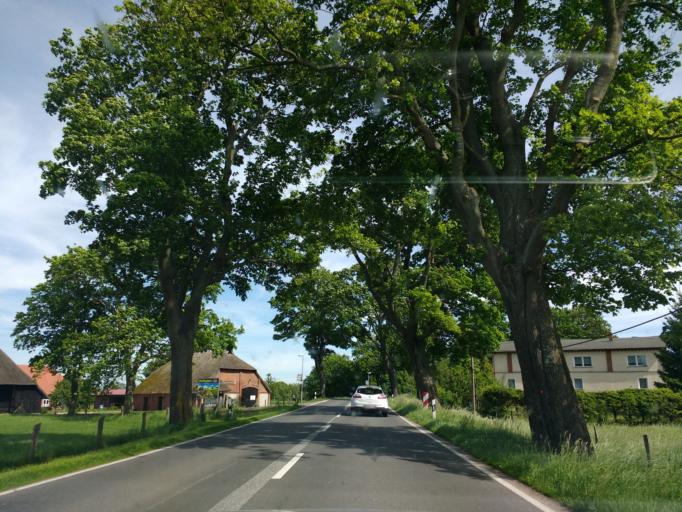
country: DE
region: Mecklenburg-Vorpommern
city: Zurow
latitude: 53.8475
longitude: 11.6388
